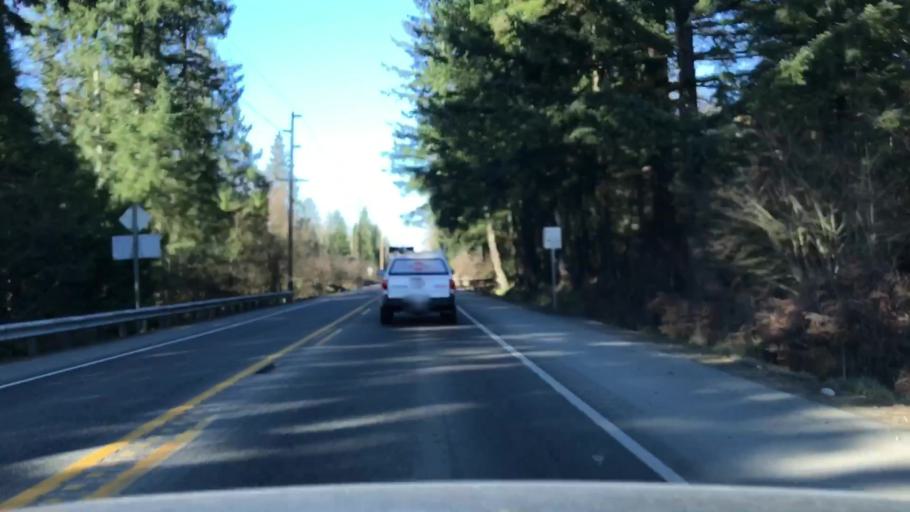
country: US
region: Washington
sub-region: King County
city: Black Diamond
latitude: 47.2896
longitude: -121.9925
